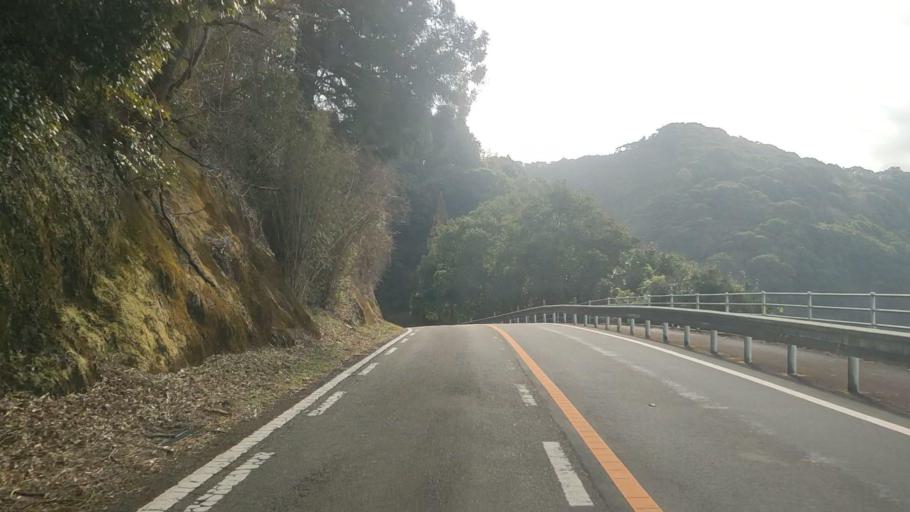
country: JP
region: Kumamoto
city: Hitoyoshi
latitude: 32.2896
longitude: 130.8455
